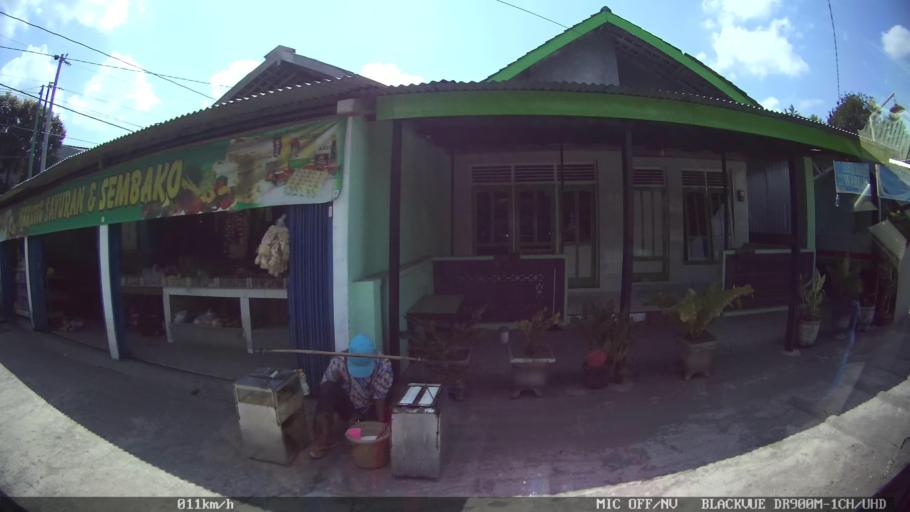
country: ID
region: Daerah Istimewa Yogyakarta
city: Sewon
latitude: -7.8433
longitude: 110.3827
